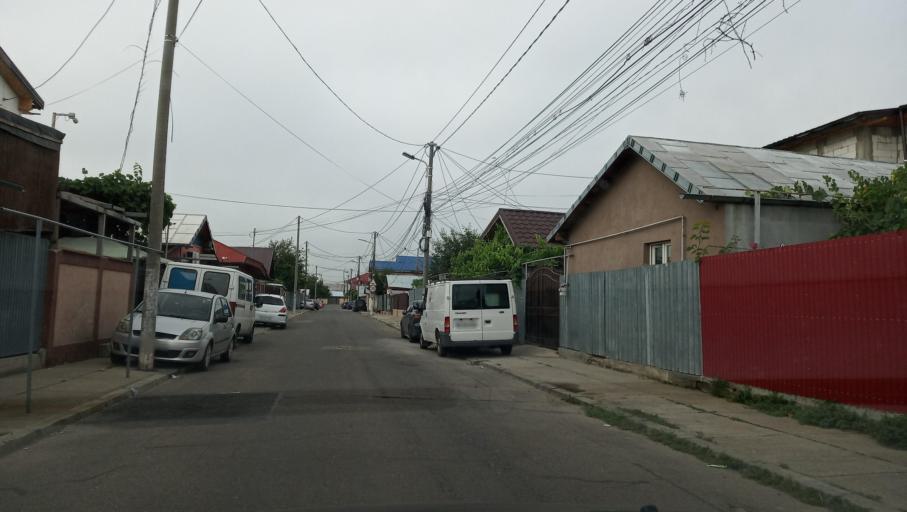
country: RO
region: Ilfov
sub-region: Comuna Glina
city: Catelu
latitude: 44.4238
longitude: 26.2045
